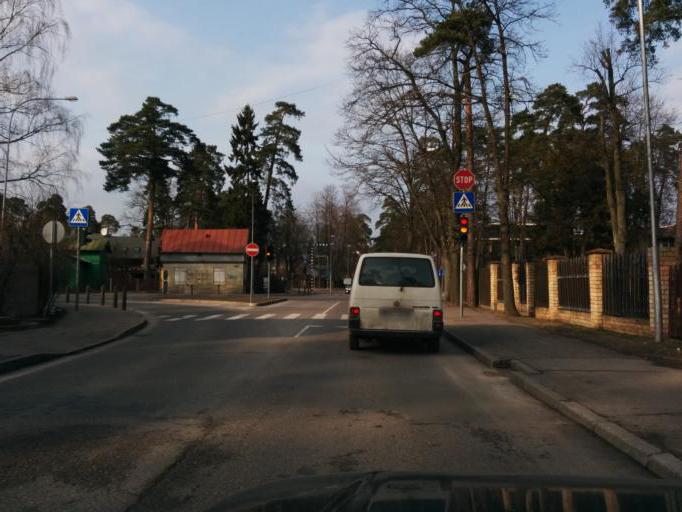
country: LV
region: Jurmala
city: Jurmala
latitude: 56.9724
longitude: 23.8140
